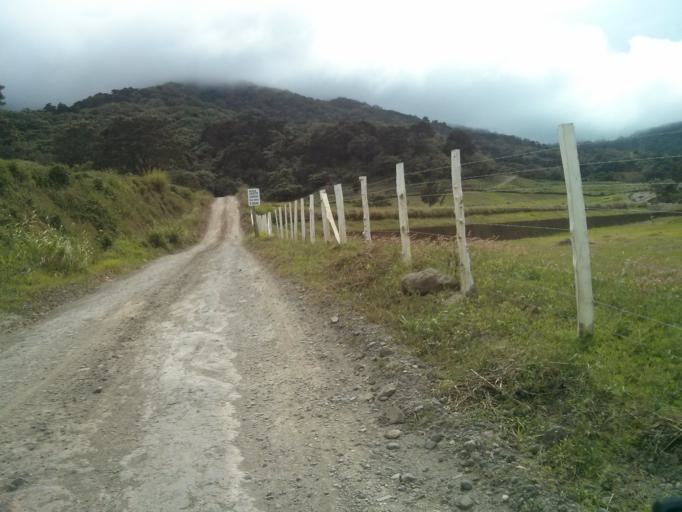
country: CR
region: Cartago
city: Tres Rios
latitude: 9.8998
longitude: -83.9881
